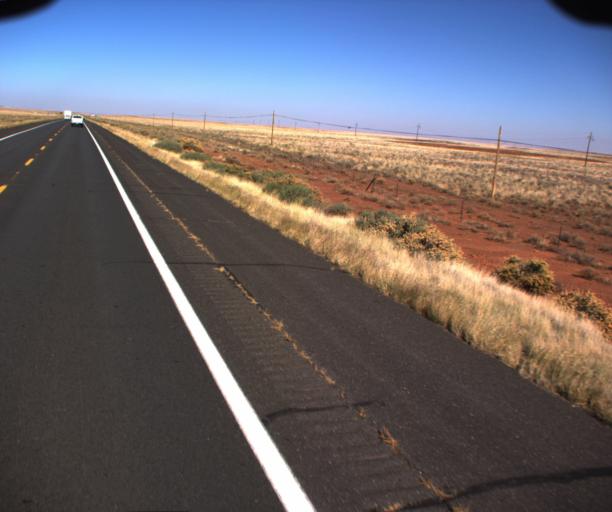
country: US
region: Arizona
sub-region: Coconino County
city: Flagstaff
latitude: 35.6687
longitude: -111.5108
